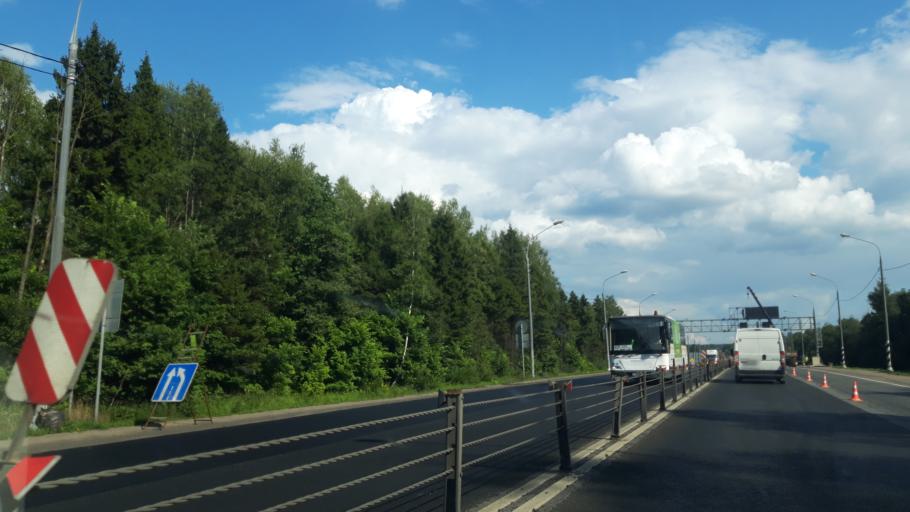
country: RU
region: Moskovskaya
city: Klin
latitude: 56.2959
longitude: 36.8024
